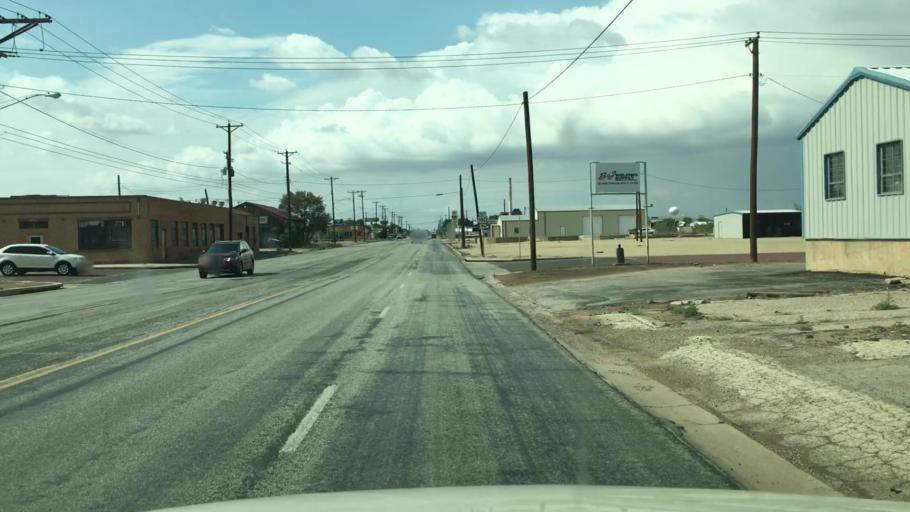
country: US
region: Texas
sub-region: Dawson County
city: Lamesa
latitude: 32.7334
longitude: -101.9491
